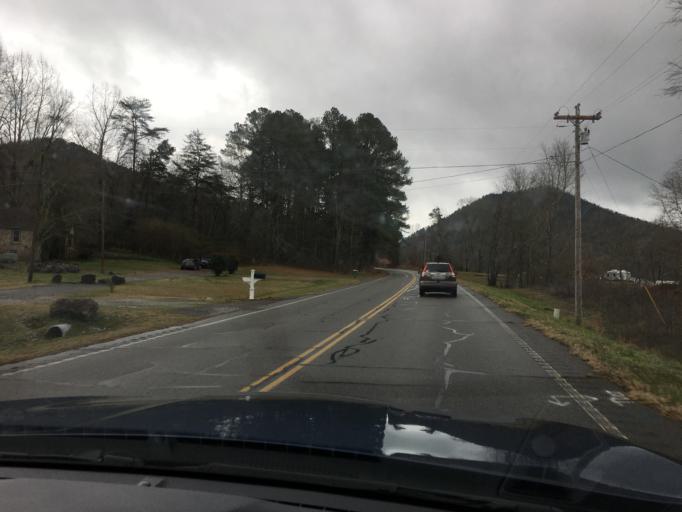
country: US
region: Tennessee
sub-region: Polk County
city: Benton
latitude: 35.1053
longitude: -84.6550
